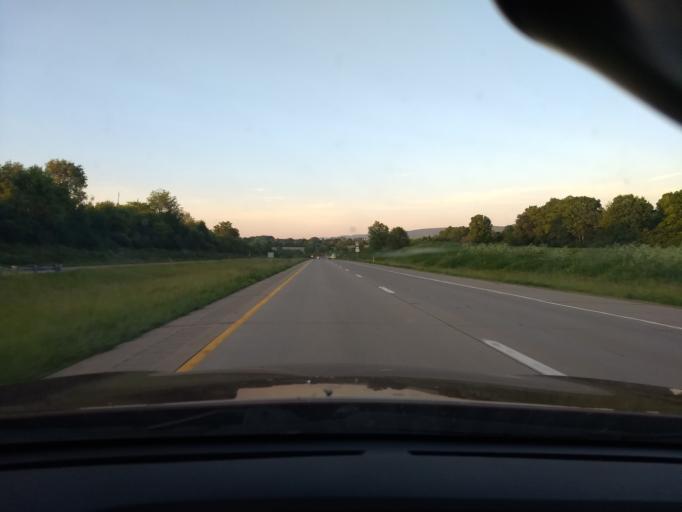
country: US
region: Pennsylvania
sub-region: Centre County
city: Pleasant Gap
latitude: 40.8775
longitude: -77.7695
